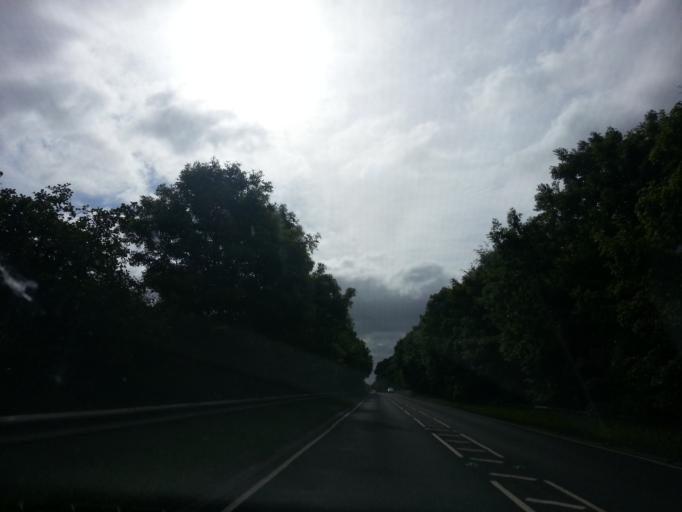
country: GB
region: England
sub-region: County Durham
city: Newton Aycliffe
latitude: 54.6560
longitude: -1.5930
